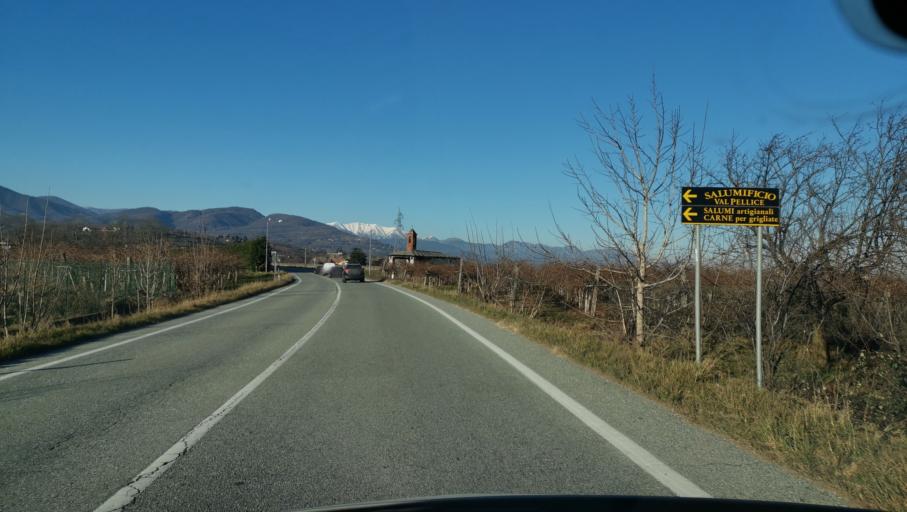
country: IT
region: Piedmont
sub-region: Provincia di Torino
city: Bibiana
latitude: 44.8005
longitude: 7.2962
